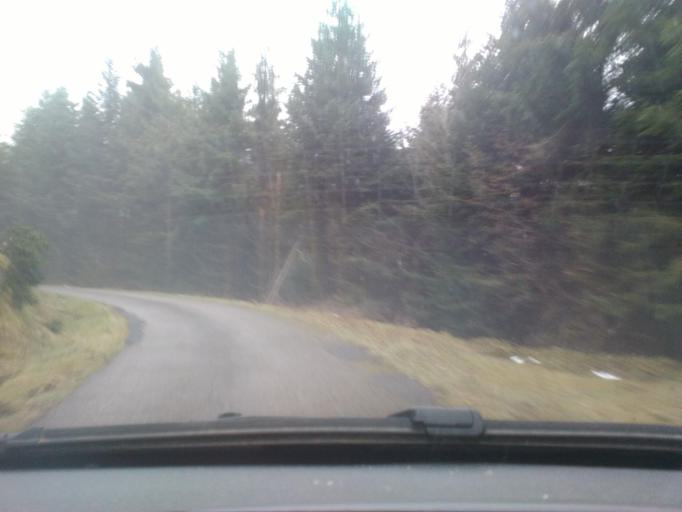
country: FR
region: Lorraine
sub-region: Departement des Vosges
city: Gerardmer
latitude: 48.1102
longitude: 6.8703
